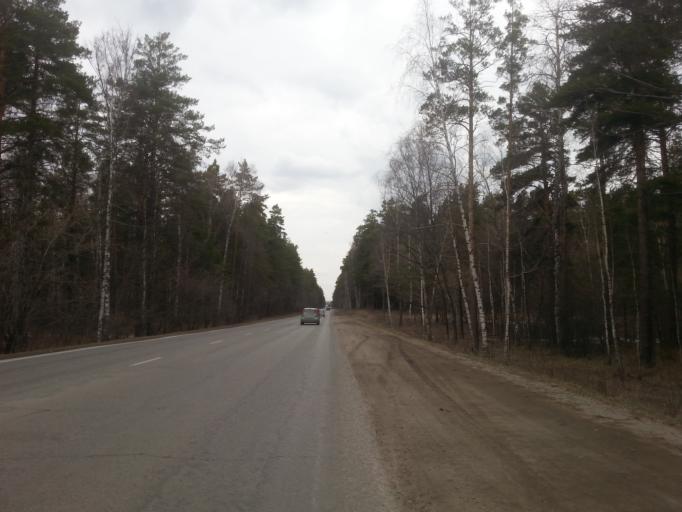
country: RU
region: Altai Krai
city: Yuzhnyy
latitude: 53.2766
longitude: 83.7200
